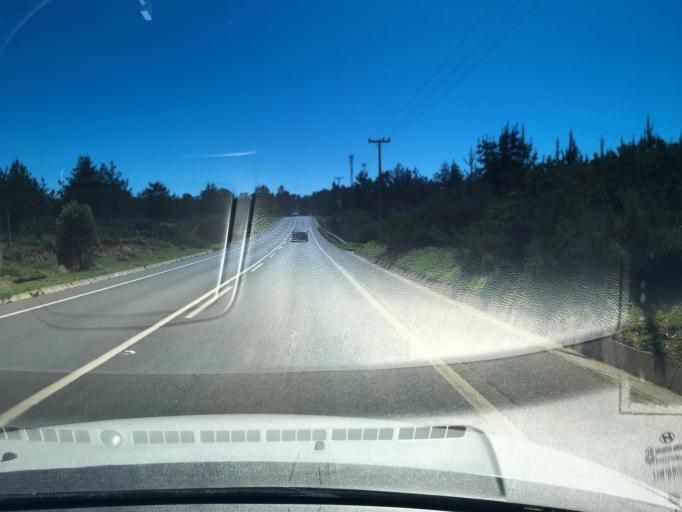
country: CL
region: Valparaiso
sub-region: San Antonio Province
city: El Tabo
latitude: -33.4281
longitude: -71.6563
